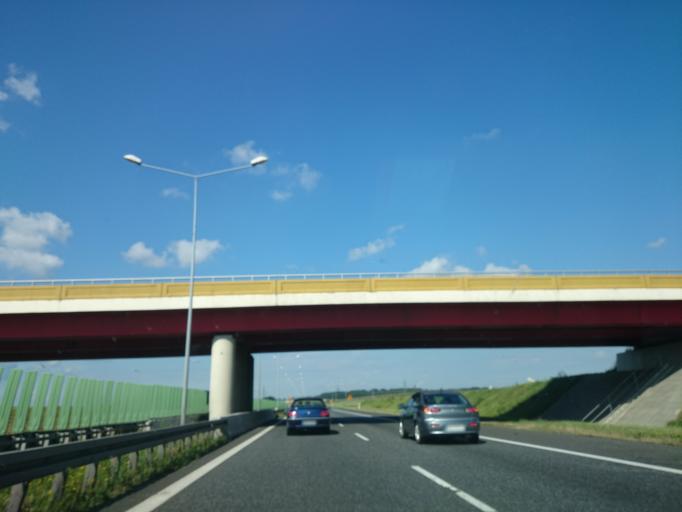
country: PL
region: Silesian Voivodeship
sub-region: Powiat gliwicki
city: Zernica
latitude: 50.2603
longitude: 18.6510
